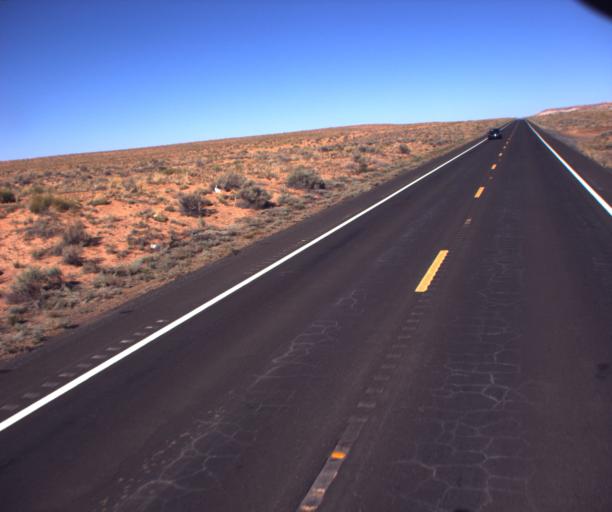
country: US
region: Arizona
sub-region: Coconino County
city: Tuba City
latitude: 36.2011
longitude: -111.0581
